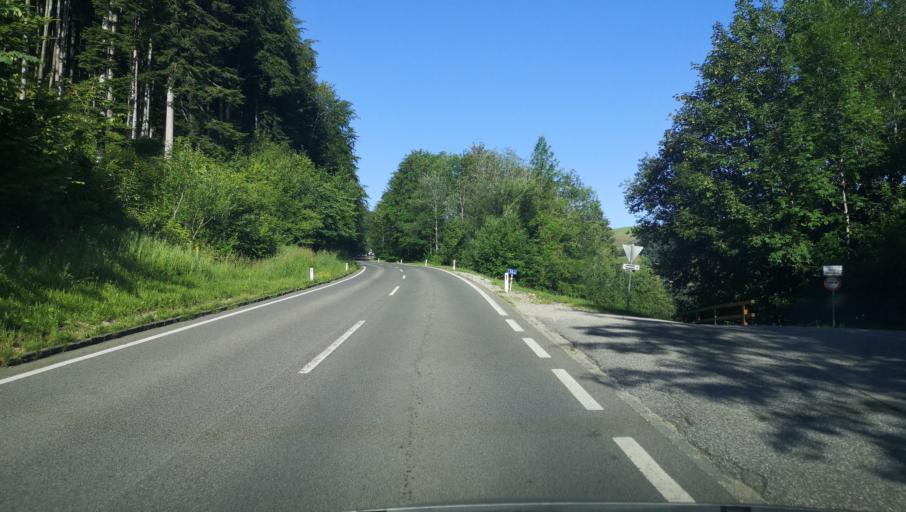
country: AT
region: Lower Austria
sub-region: Politischer Bezirk Scheibbs
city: Gresten
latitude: 47.9730
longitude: 14.9882
